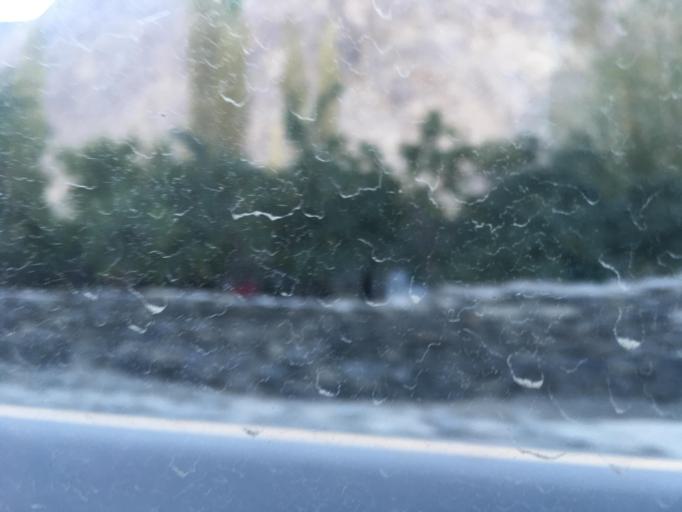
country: PK
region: Gilgit-Baltistan
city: Skardu
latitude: 35.3589
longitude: 75.5086
